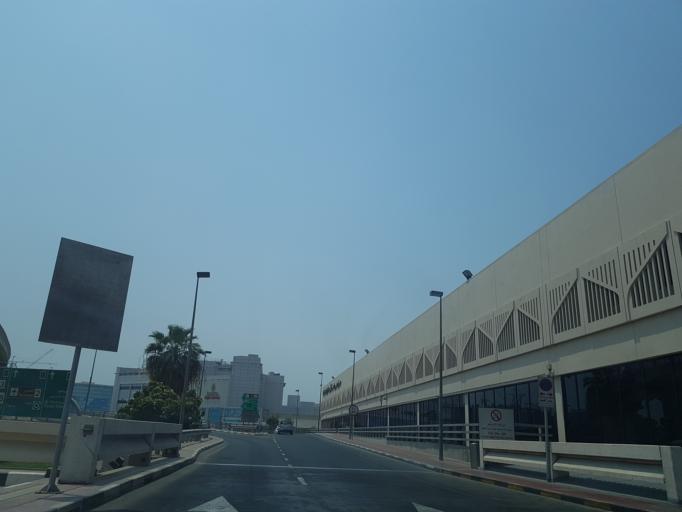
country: AE
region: Ash Shariqah
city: Sharjah
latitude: 25.2496
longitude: 55.3511
